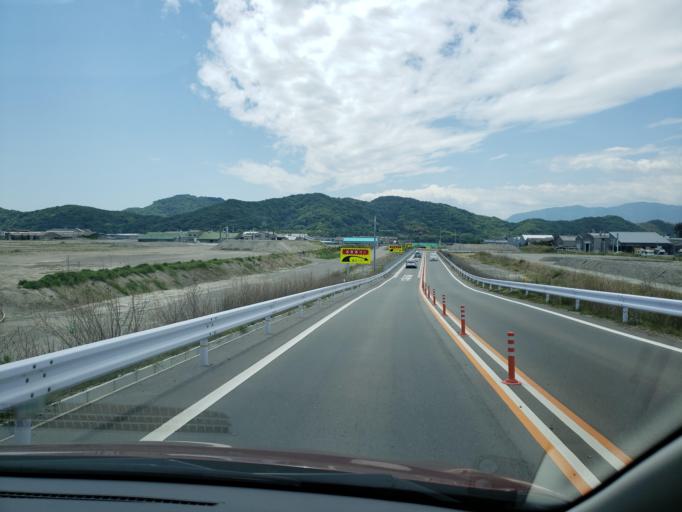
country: JP
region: Tokushima
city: Tokushima-shi
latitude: 34.0458
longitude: 134.5847
